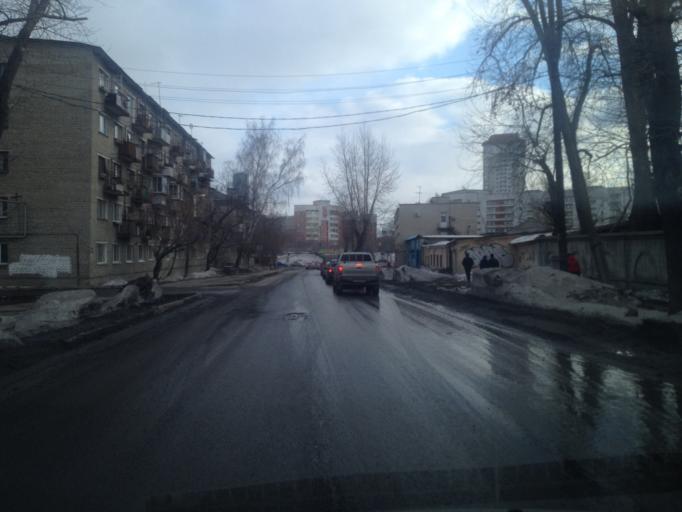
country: RU
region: Sverdlovsk
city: Yekaterinburg
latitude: 56.8572
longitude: 60.5813
